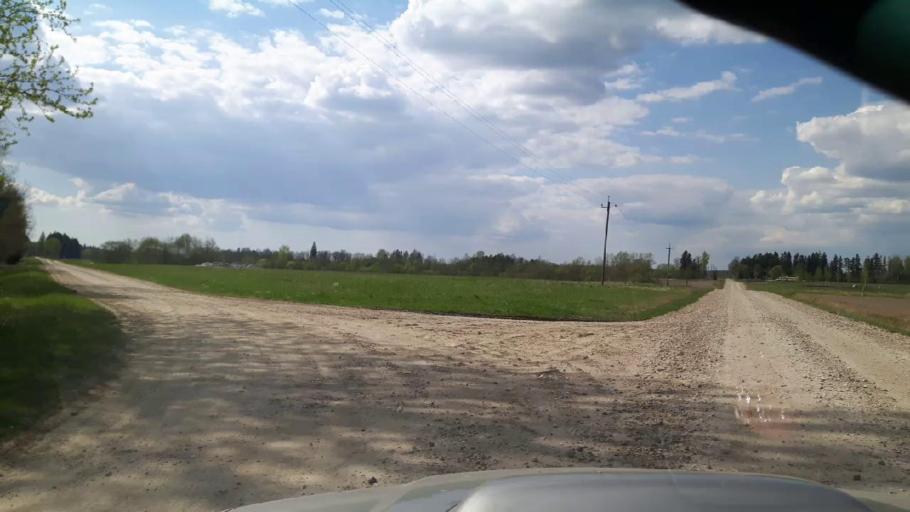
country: EE
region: Paernumaa
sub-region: Sindi linn
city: Sindi
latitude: 58.4336
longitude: 24.7929
